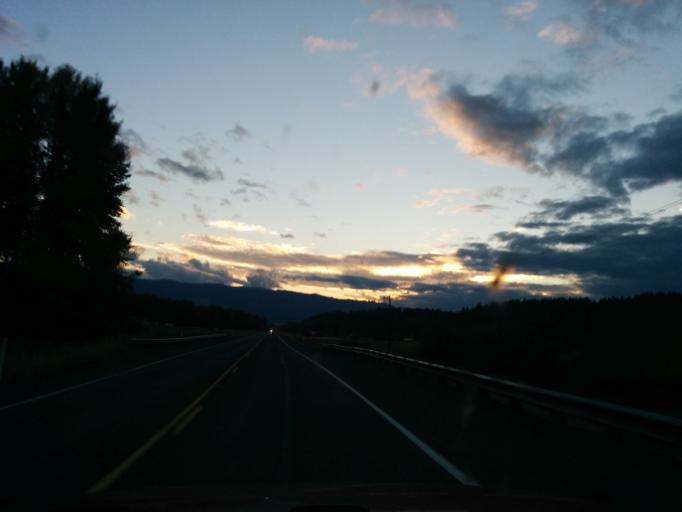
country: US
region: Washington
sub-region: Kittitas County
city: Cle Elum
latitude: 47.1926
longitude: -120.8093
